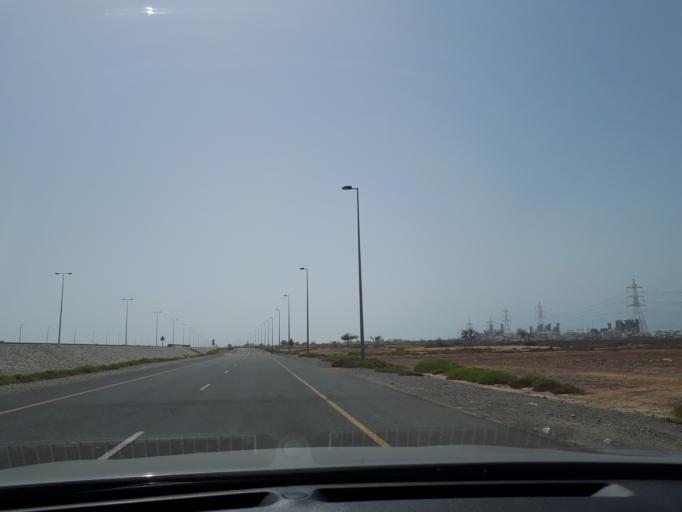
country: OM
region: Al Batinah
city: Barka'
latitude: 23.7006
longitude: 57.9957
